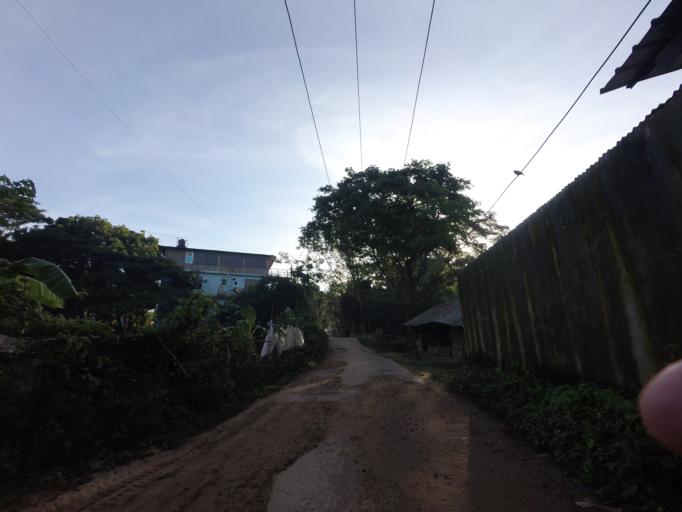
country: BD
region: Chittagong
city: Fatikchari
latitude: 22.5820
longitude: 91.6864
